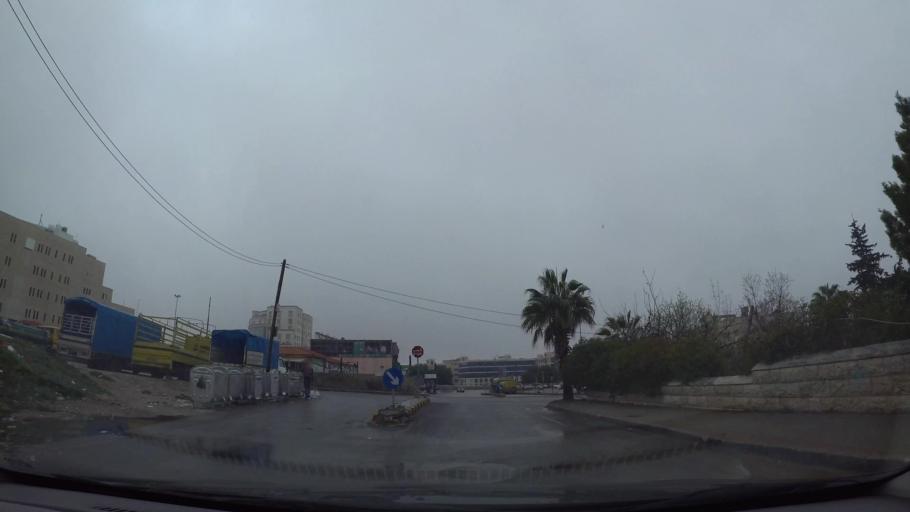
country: JO
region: Amman
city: Wadi as Sir
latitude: 31.9605
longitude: 35.8562
